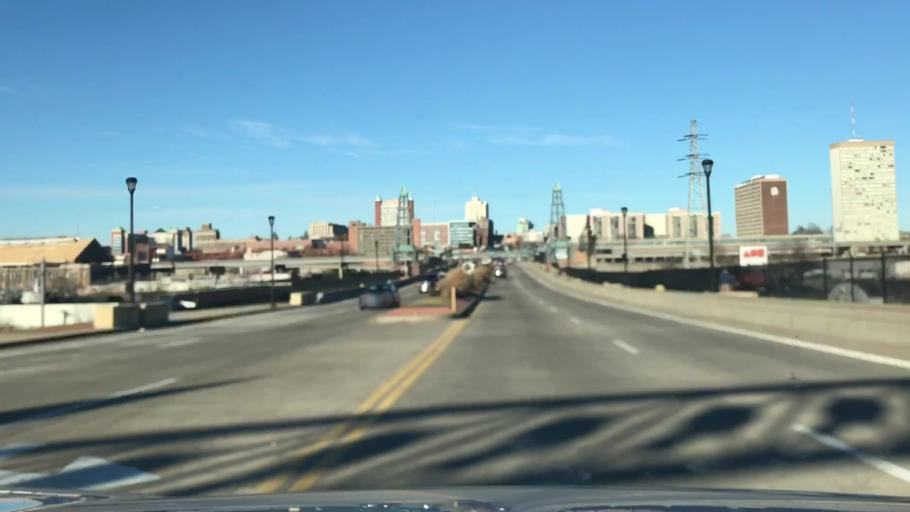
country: US
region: Missouri
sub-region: City of Saint Louis
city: St. Louis
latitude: 38.6272
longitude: -90.2363
